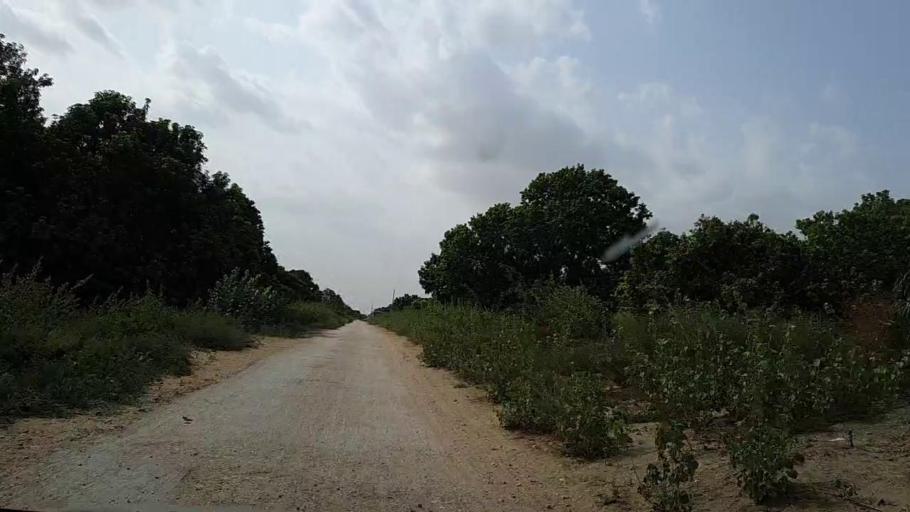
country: PK
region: Sindh
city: Kotri
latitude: 25.2431
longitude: 68.2632
